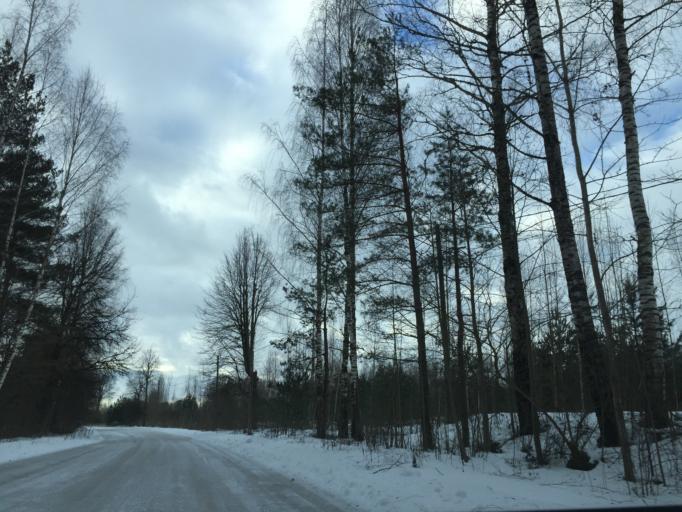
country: LV
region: Lielvarde
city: Lielvarde
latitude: 56.5739
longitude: 24.7350
